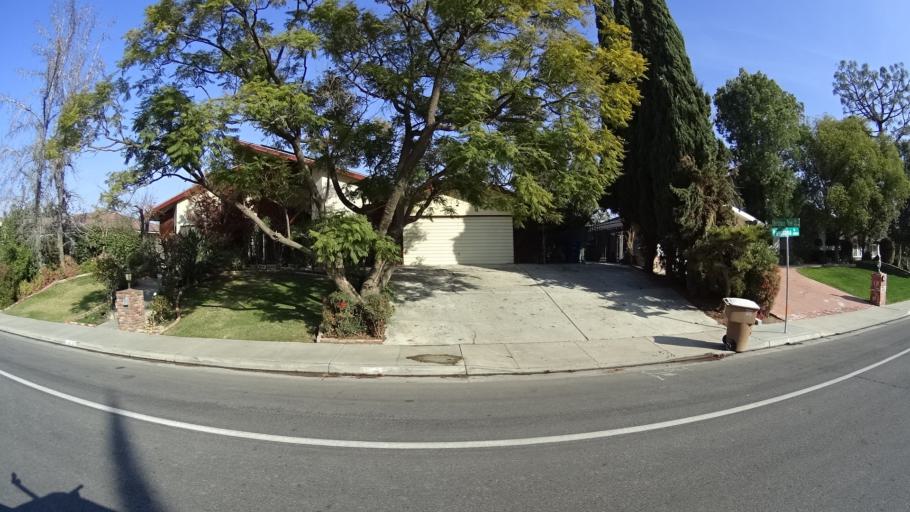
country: US
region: California
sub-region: Kern County
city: Oildale
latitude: 35.4078
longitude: -118.9391
